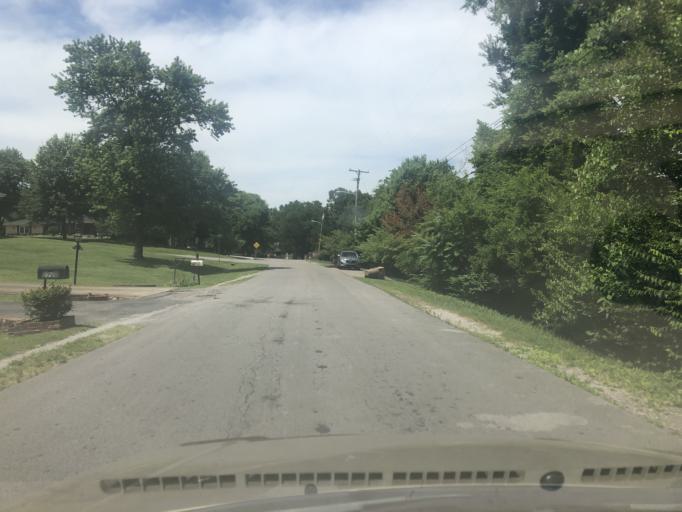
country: US
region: Tennessee
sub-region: Davidson County
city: Lakewood
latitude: 36.1898
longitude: -86.6707
